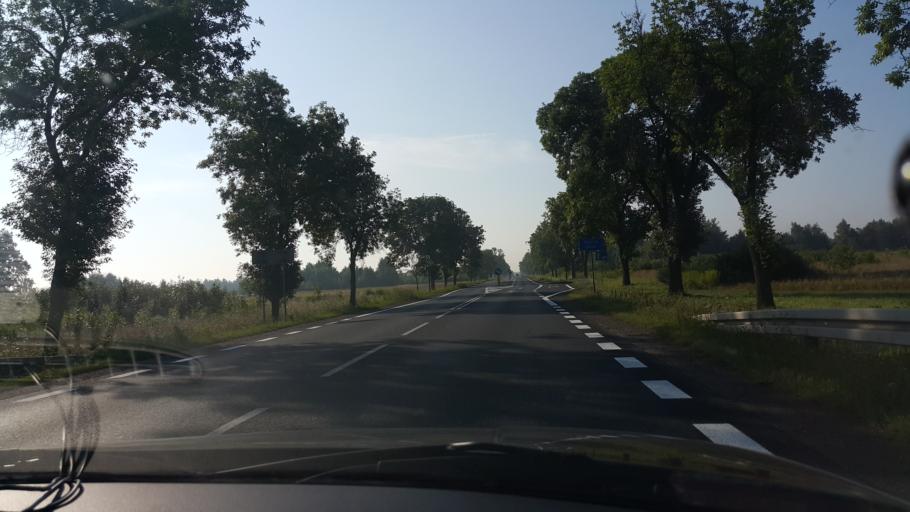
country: PL
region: Masovian Voivodeship
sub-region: Powiat radomski
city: Jedlnia-Letnisko
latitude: 51.3991
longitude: 21.2584
